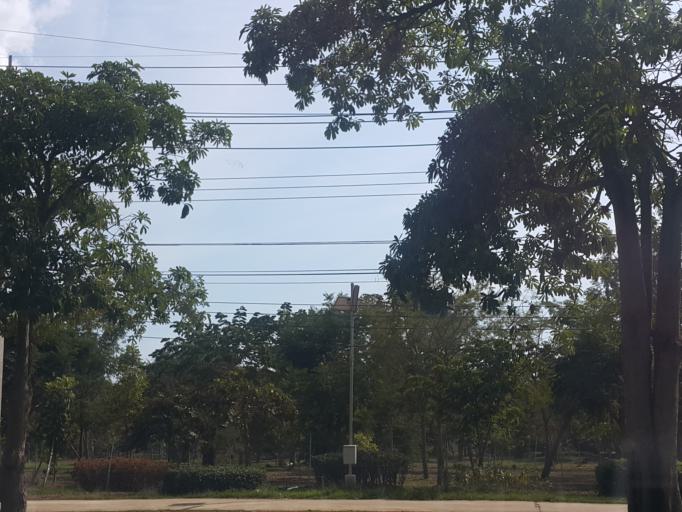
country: TH
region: Sukhothai
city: Si Samrong
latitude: 17.2279
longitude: 99.8254
